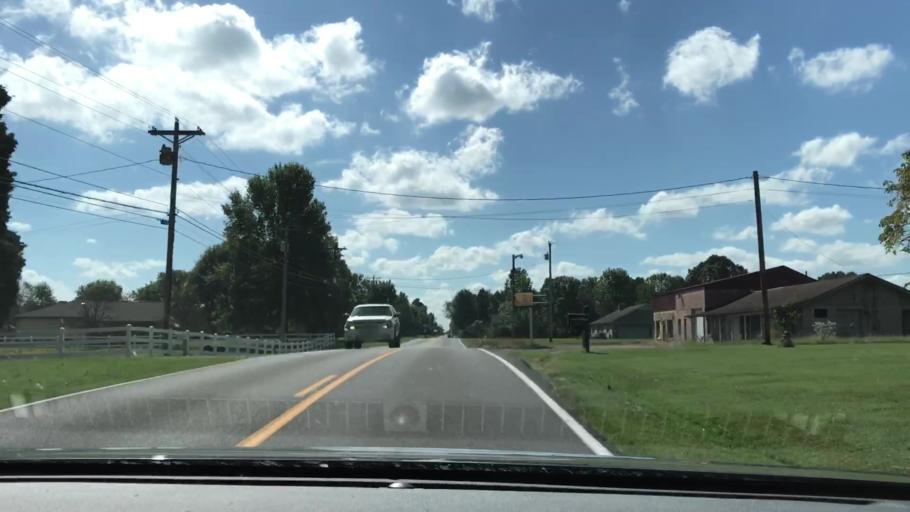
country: US
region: Kentucky
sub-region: McCracken County
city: Reidland
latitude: 36.9282
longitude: -88.5188
